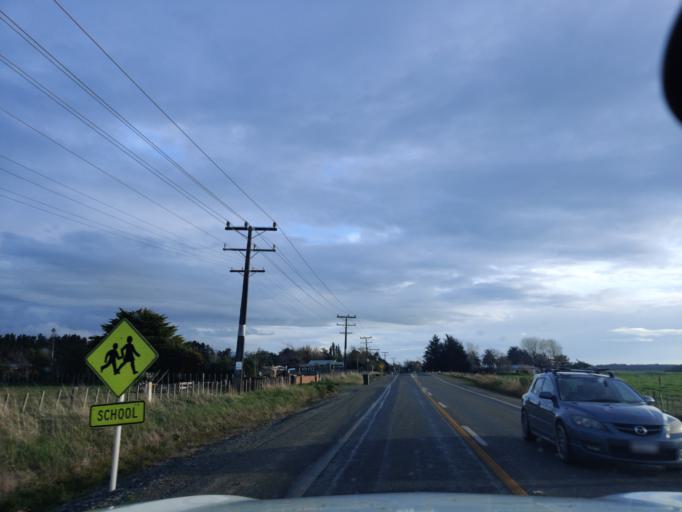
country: NZ
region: Manawatu-Wanganui
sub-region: Palmerston North City
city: Palmerston North
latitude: -40.3982
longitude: 175.6238
